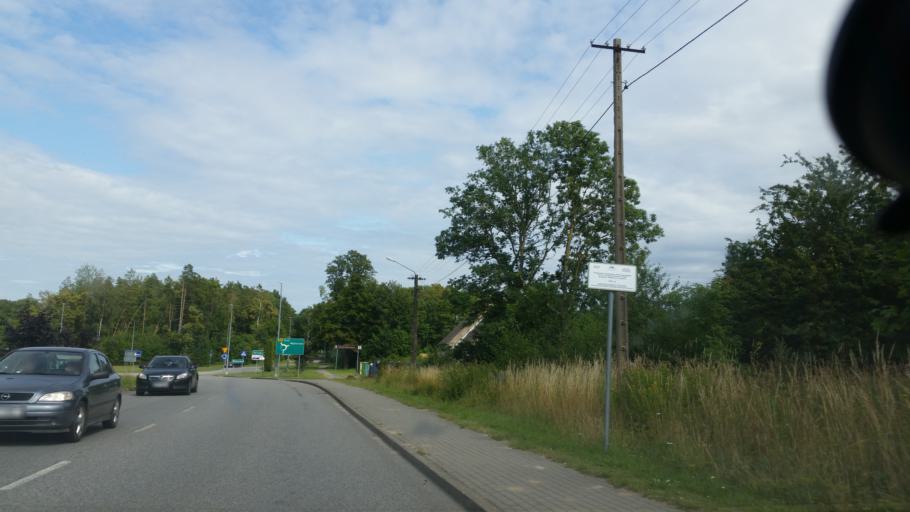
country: PL
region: Pomeranian Voivodeship
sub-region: Powiat wejherowski
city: Choczewo
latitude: 54.7246
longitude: 17.8638
